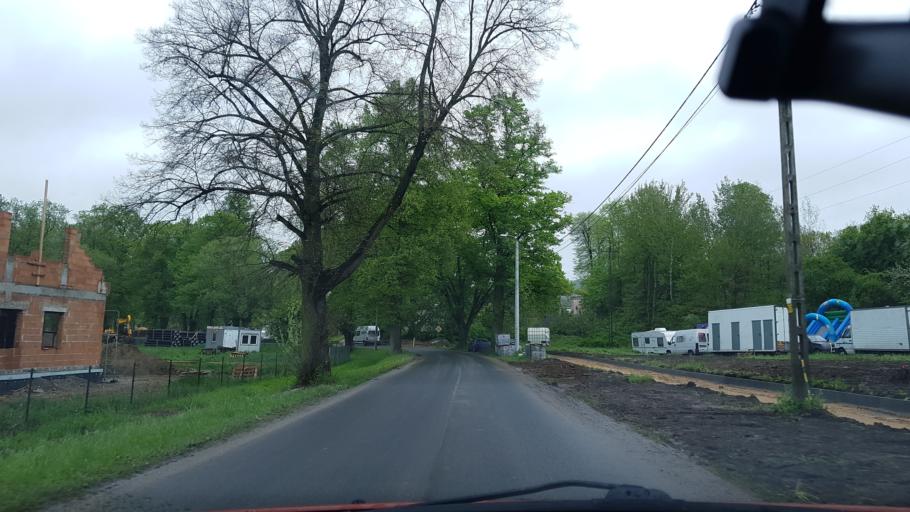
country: PL
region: Lower Silesian Voivodeship
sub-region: Powiat dzierzoniowski
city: Niemcza
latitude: 50.7138
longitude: 16.8411
